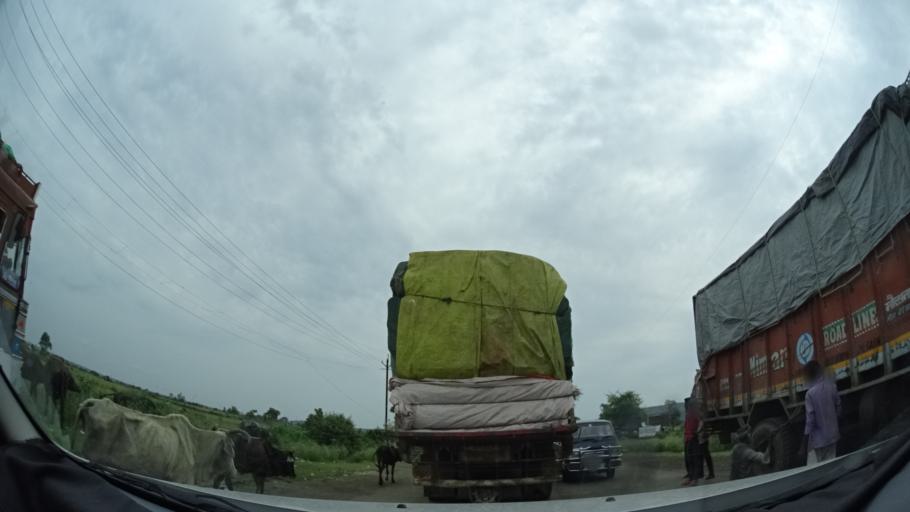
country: IN
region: Madhya Pradesh
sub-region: Raisen
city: Sultanpur
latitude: 23.3226
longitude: 78.0920
